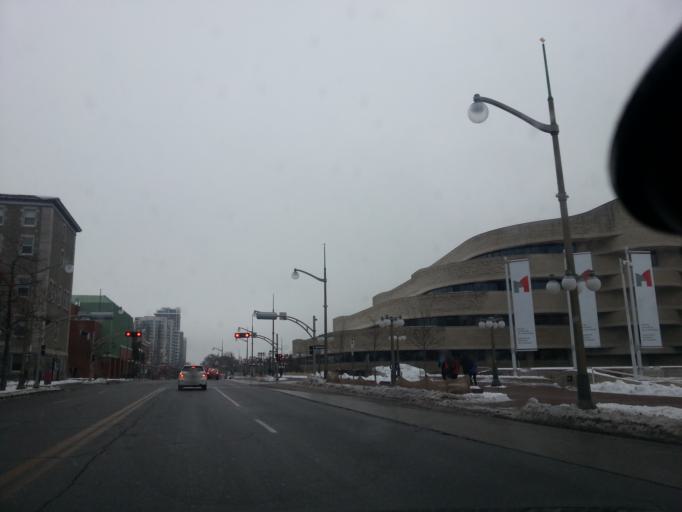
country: CA
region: Ontario
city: Ottawa
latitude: 45.4303
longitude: -75.7100
